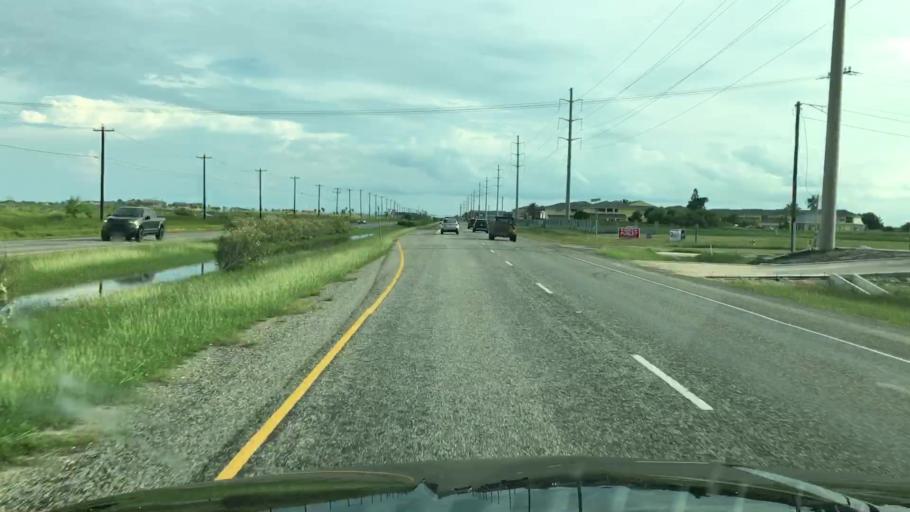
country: US
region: Texas
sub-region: Nueces County
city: Corpus Christi
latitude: 27.6148
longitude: -97.2219
